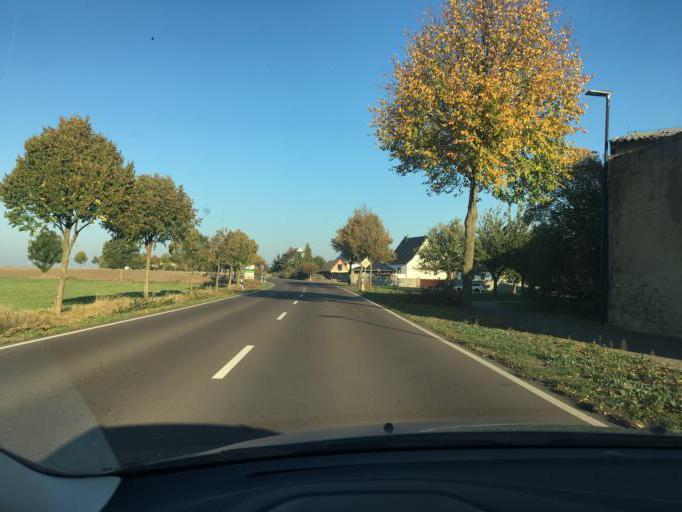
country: DE
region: Saxony-Anhalt
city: Welsleben
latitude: 52.0021
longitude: 11.6307
